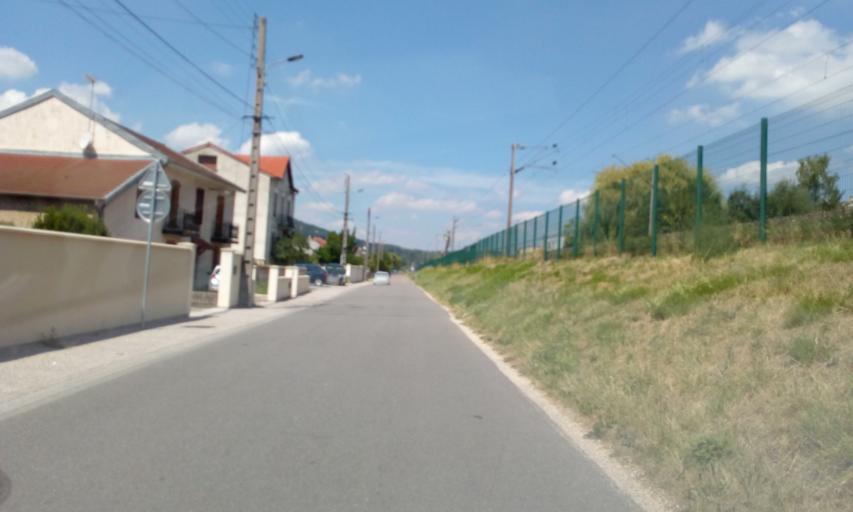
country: FR
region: Lorraine
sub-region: Departement de Meurthe-et-Moselle
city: Maidieres
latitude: 48.9056
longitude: 6.0471
